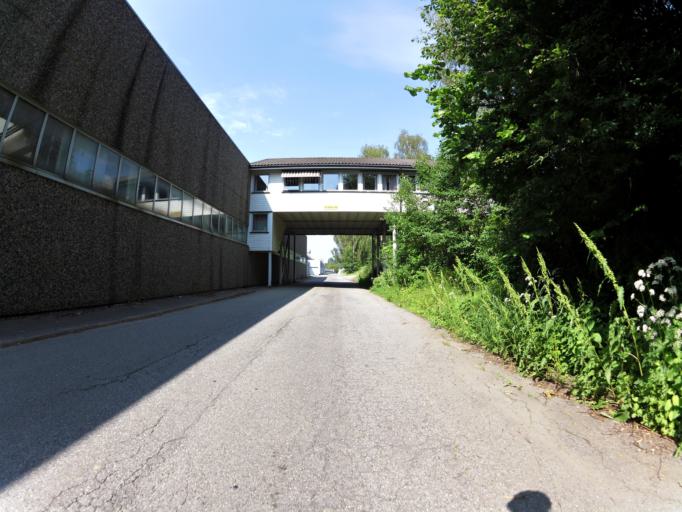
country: NO
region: Ostfold
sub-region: Sarpsborg
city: Sarpsborg
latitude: 59.2710
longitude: 11.1263
